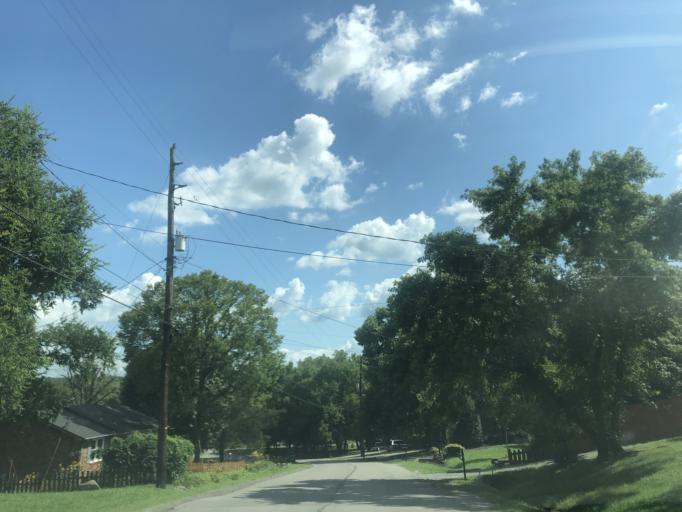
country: US
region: Tennessee
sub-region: Wilson County
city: Green Hill
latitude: 36.2072
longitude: -86.5873
